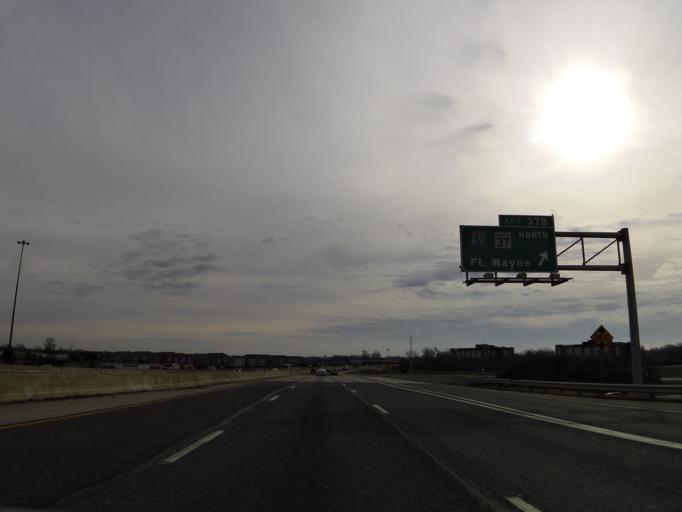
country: US
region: Indiana
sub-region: Marion County
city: Lawrence
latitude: 39.8954
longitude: -86.0550
